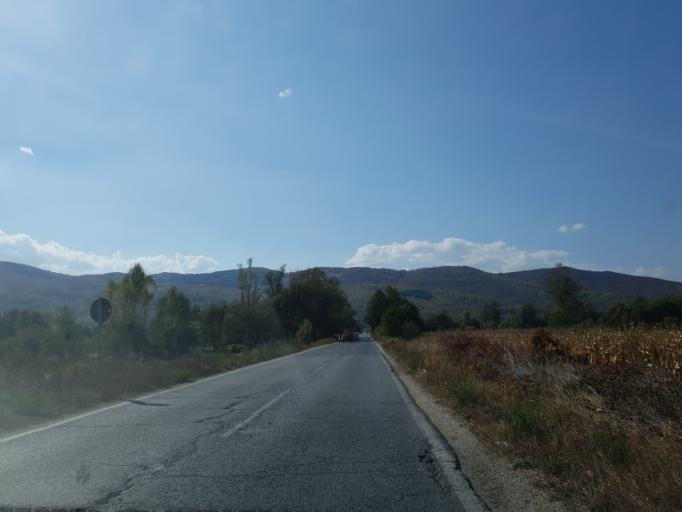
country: MK
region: Kicevo
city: Kicevo
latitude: 41.4811
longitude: 20.9922
